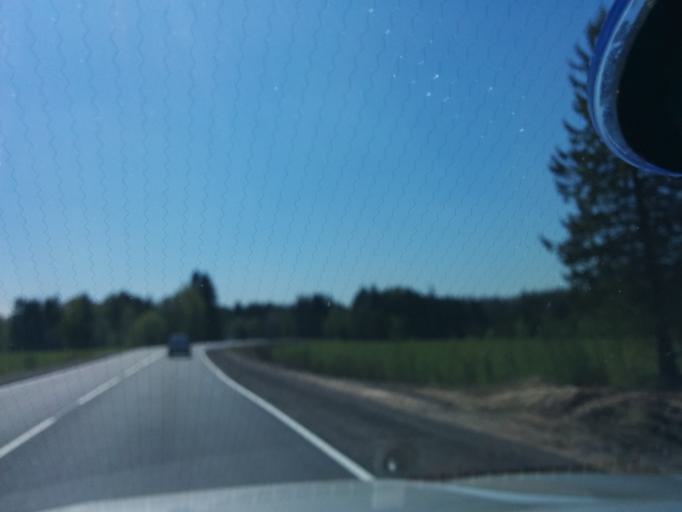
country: RU
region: Leningrad
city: Verkhniye Osel'ki
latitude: 60.2014
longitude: 30.4262
